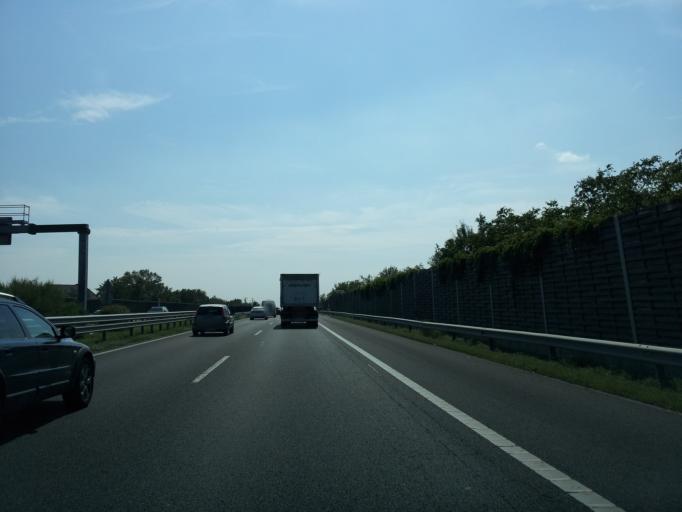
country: HU
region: Pest
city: Erd
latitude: 47.4080
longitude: 18.8760
